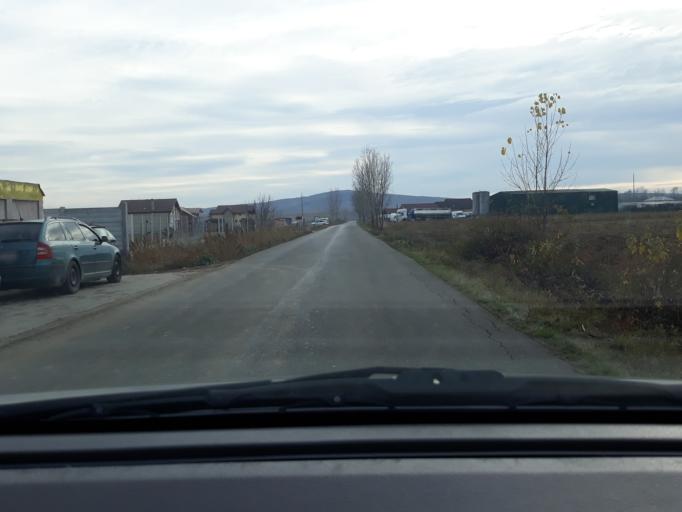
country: RO
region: Bihor
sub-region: Comuna Sanmartin
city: Sanmartin
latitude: 47.0255
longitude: 22.0035
